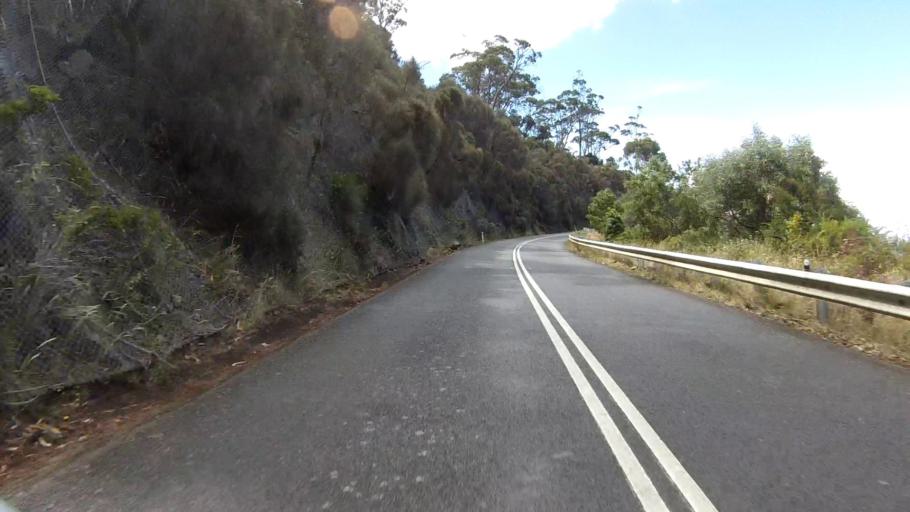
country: AU
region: Tasmania
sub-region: Sorell
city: Sorell
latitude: -42.2267
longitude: 148.0249
